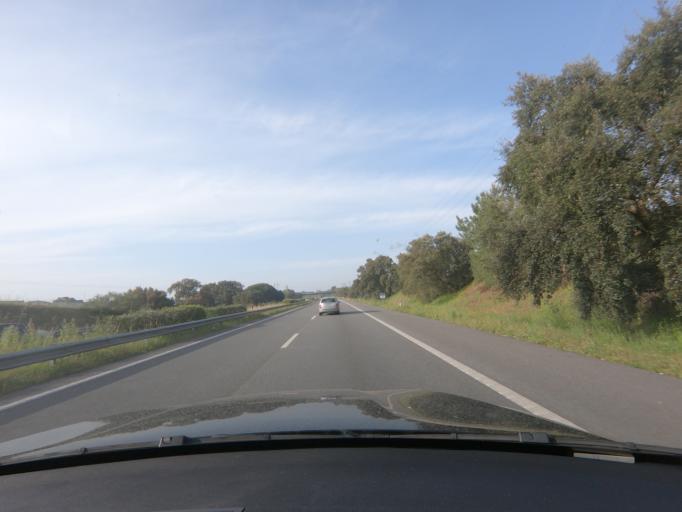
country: PT
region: Setubal
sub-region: Palmela
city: Palmela
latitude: 38.5560
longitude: -8.8700
